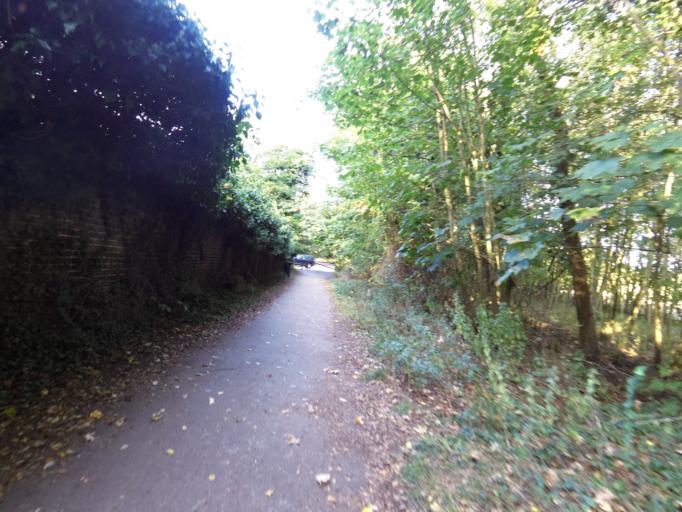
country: GB
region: England
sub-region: Suffolk
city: Kesgrave
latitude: 52.0060
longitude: 1.2327
